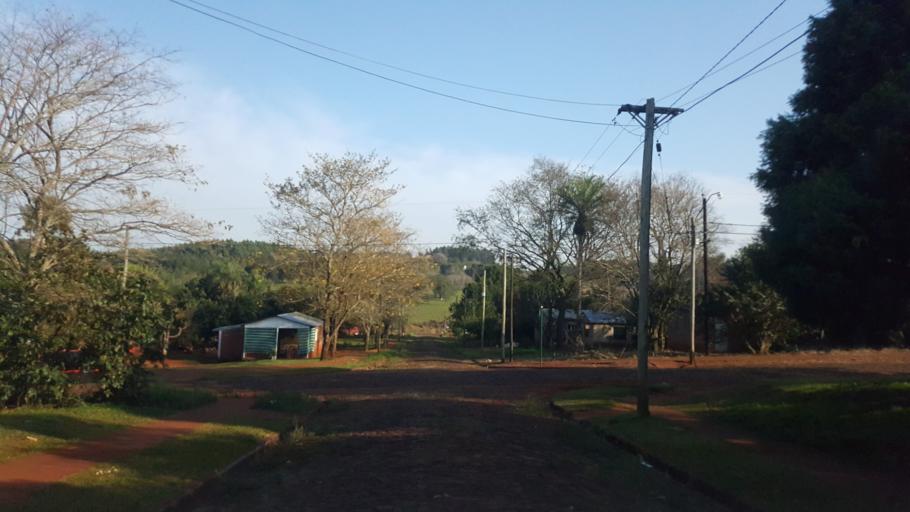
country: AR
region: Misiones
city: Capiovi
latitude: -26.8919
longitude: -55.0719
